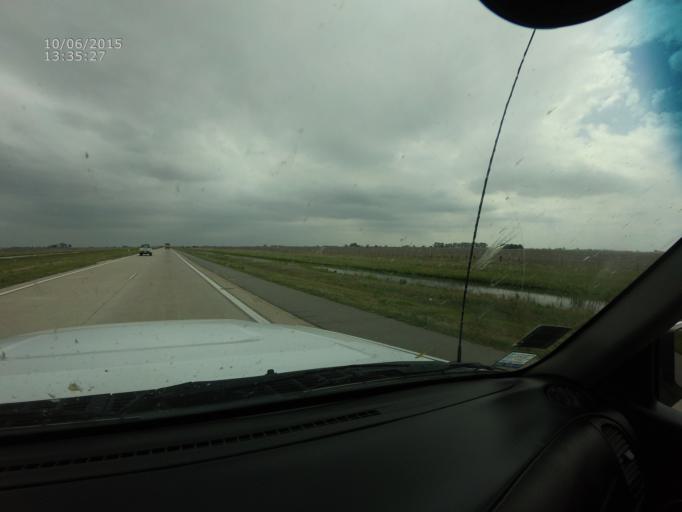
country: AR
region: Cordoba
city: Leones
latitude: -32.6161
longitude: -62.3716
